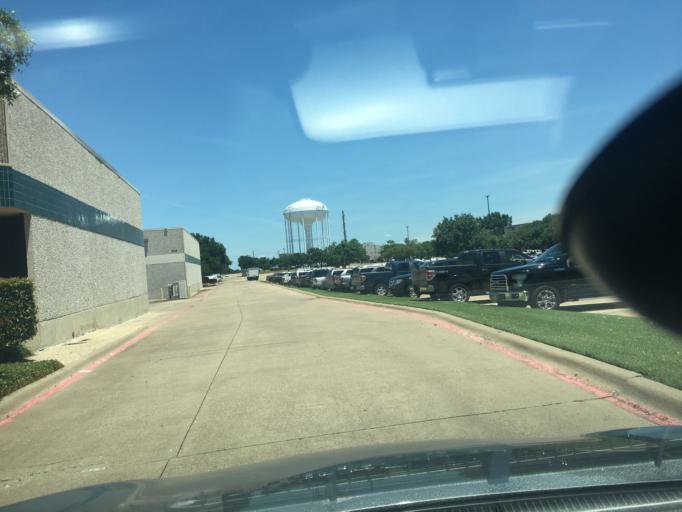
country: US
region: Texas
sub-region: Dallas County
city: Richardson
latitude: 32.9557
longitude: -96.7084
